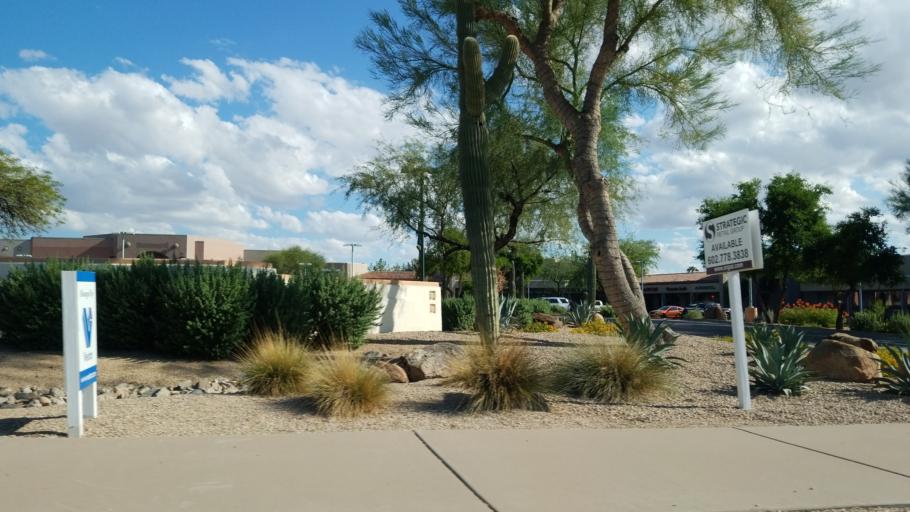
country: US
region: Arizona
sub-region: Maricopa County
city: Scottsdale
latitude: 33.5876
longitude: -111.8388
